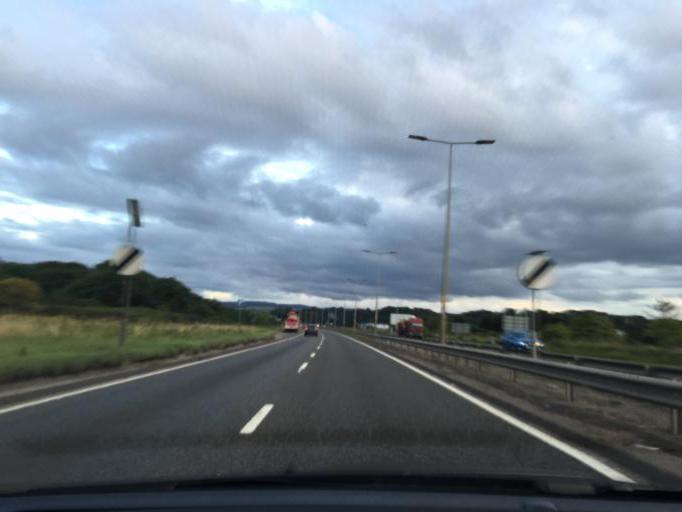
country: GB
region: Scotland
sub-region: Highland
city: Inverness
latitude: 57.4883
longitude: -4.2093
